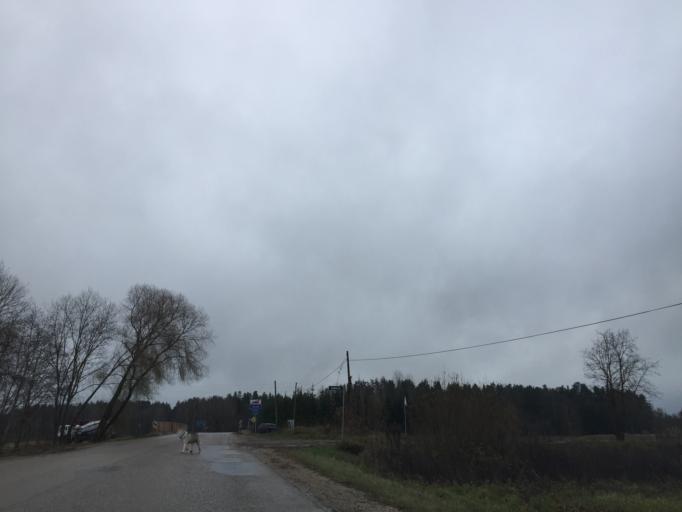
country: LV
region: Adazi
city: Adazi
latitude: 57.0663
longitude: 24.3617
